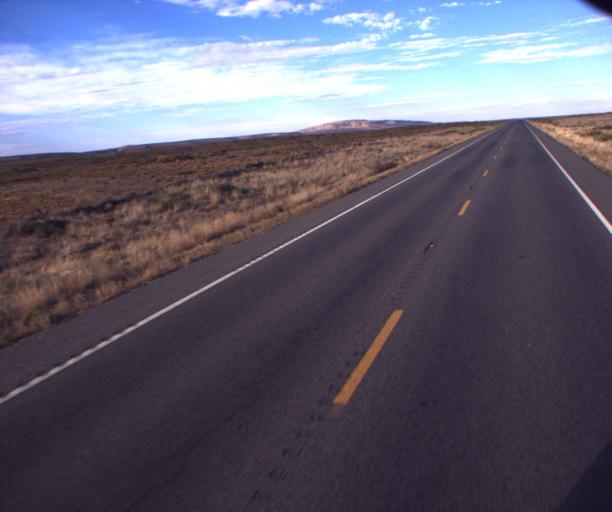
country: US
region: Arizona
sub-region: Apache County
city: Lukachukai
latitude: 36.9288
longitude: -109.2041
